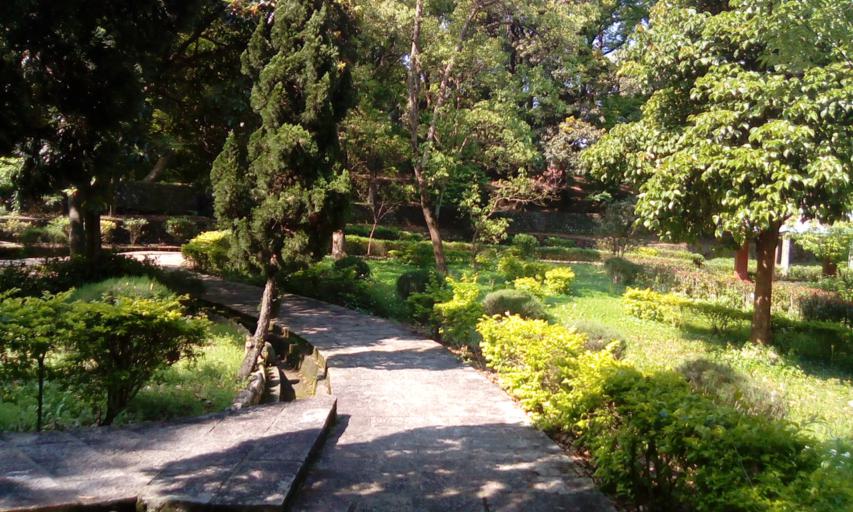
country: TW
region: Taipei
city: Taipei
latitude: 25.2018
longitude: 121.4820
